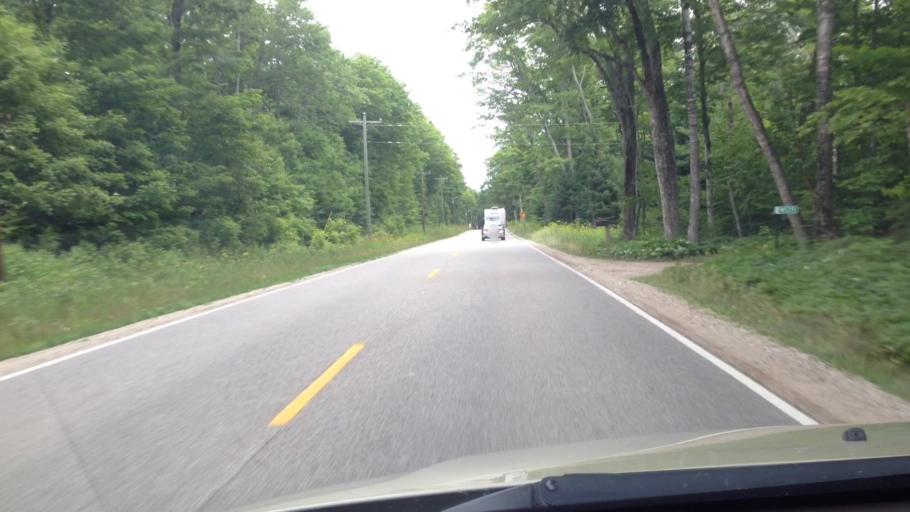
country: US
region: Michigan
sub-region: Mackinac County
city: Saint Ignace
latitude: 46.0569
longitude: -85.1204
